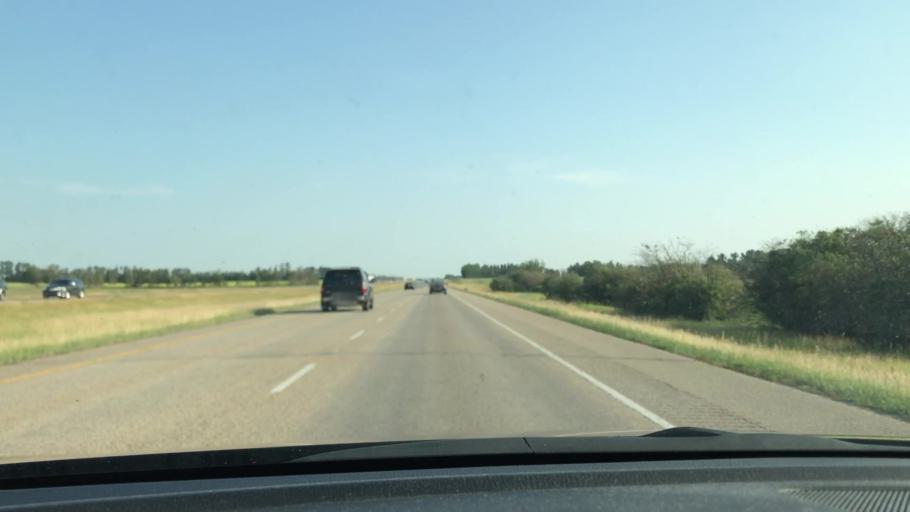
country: CA
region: Alberta
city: Millet
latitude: 53.1191
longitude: -113.5984
